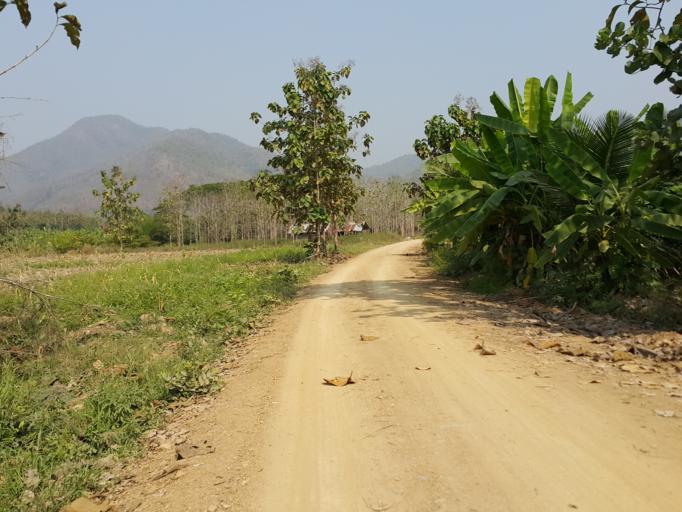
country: TH
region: Sukhothai
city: Thung Saliam
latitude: 17.3395
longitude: 99.4646
